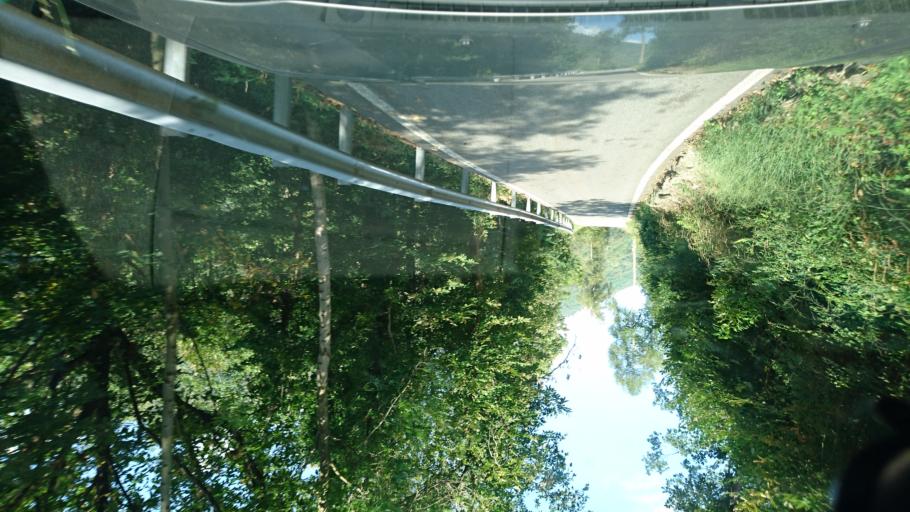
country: IT
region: Lombardy
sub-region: Provincia di Brescia
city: Berzo
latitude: 46.0918
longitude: 10.3115
